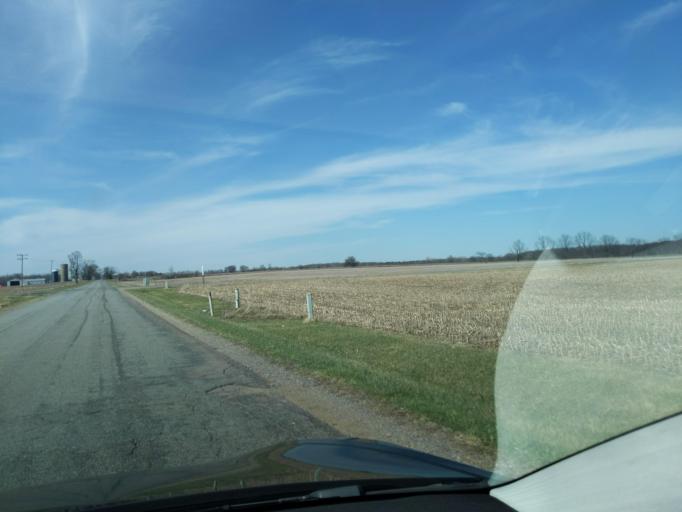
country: US
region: Michigan
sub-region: Ingham County
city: Williamston
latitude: 42.6289
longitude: -84.3100
